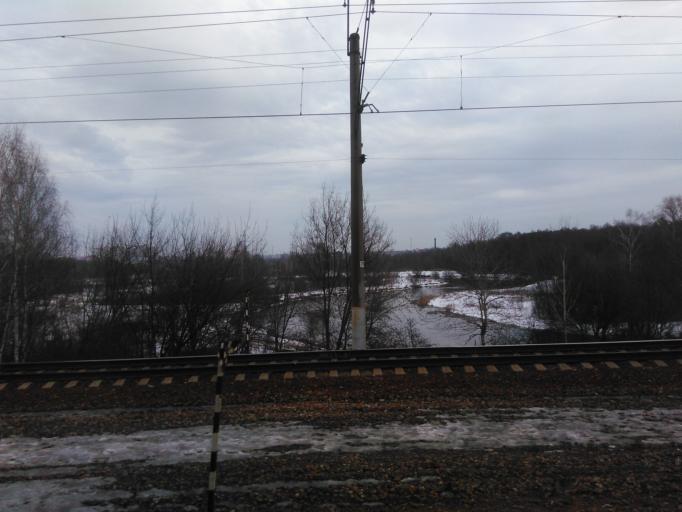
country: RU
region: Moskovskaya
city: Mamontovka
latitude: 55.9975
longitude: 37.8309
